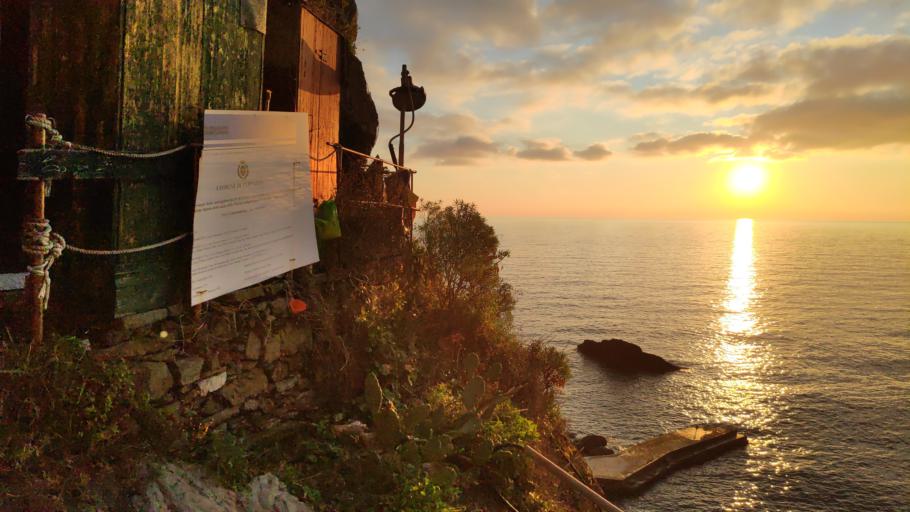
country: IT
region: Liguria
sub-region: Provincia di La Spezia
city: Vernazza
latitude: 44.1201
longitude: 9.7056
